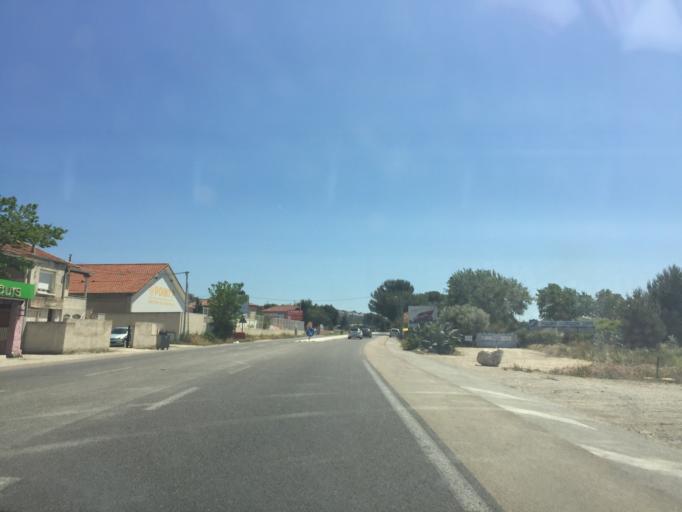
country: FR
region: Provence-Alpes-Cote d'Azur
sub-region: Departement des Bouches-du-Rhone
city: Rognac
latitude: 43.4845
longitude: 5.2235
